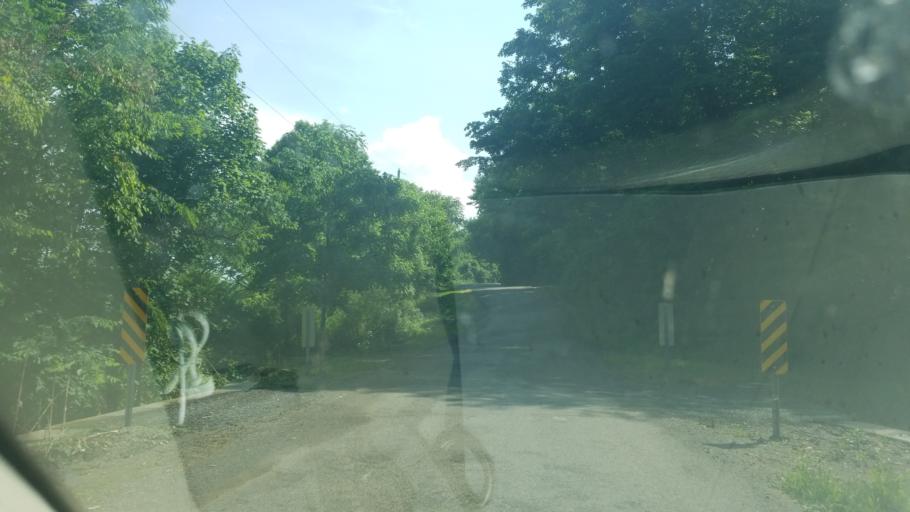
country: US
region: Ohio
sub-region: Champaign County
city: North Lewisburg
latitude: 40.2782
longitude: -83.6422
